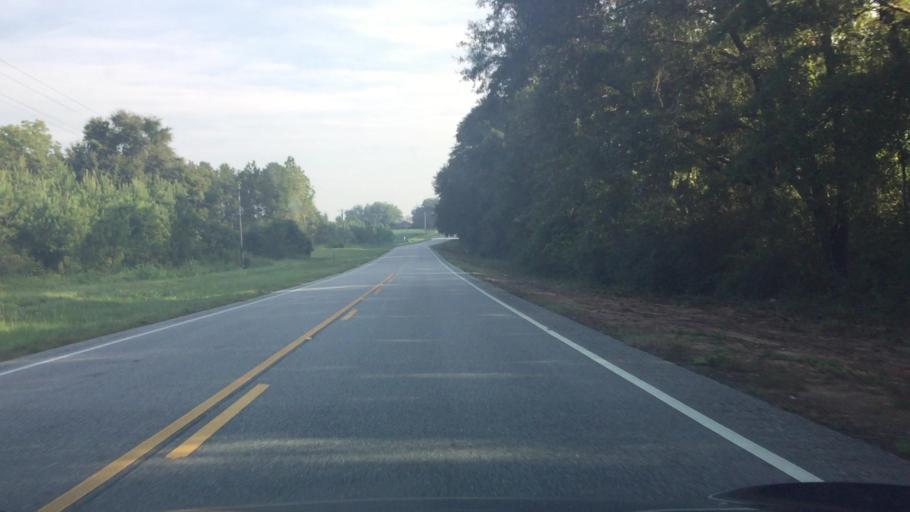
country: US
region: Alabama
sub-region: Covington County
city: Andalusia
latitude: 31.1649
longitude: -86.4597
